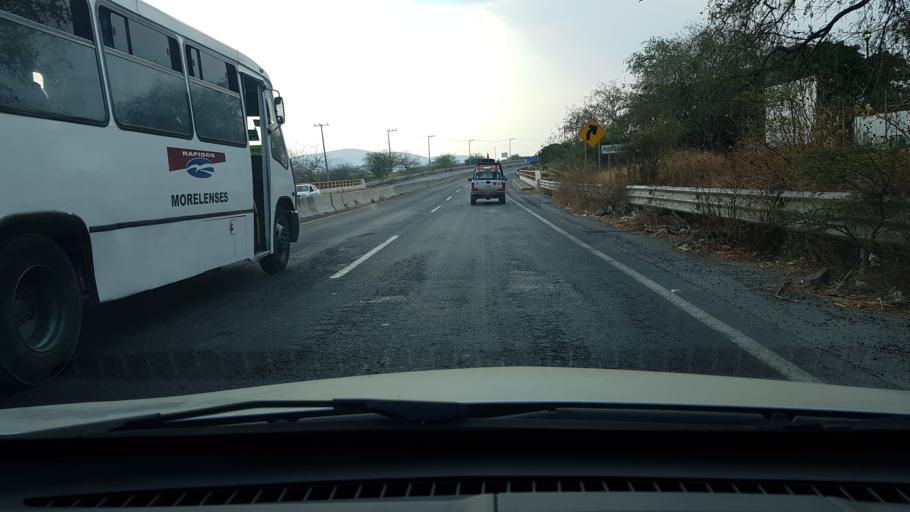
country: MX
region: Morelos
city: Amayuca
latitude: 18.7206
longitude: -98.8016
